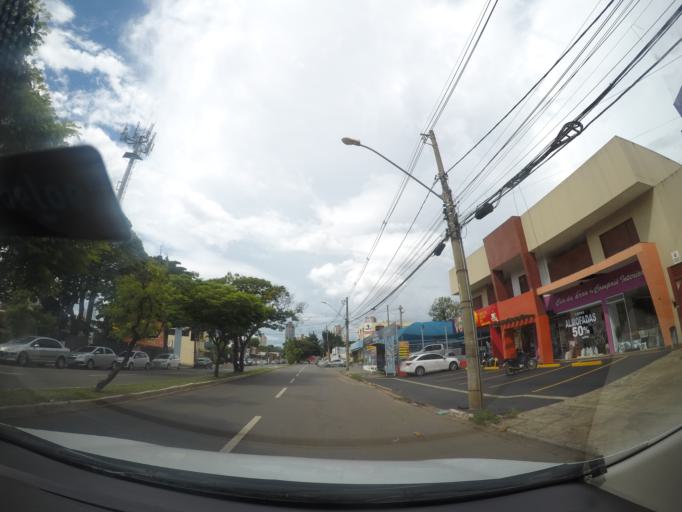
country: BR
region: Goias
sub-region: Goiania
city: Goiania
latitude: -16.6955
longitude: -49.2747
